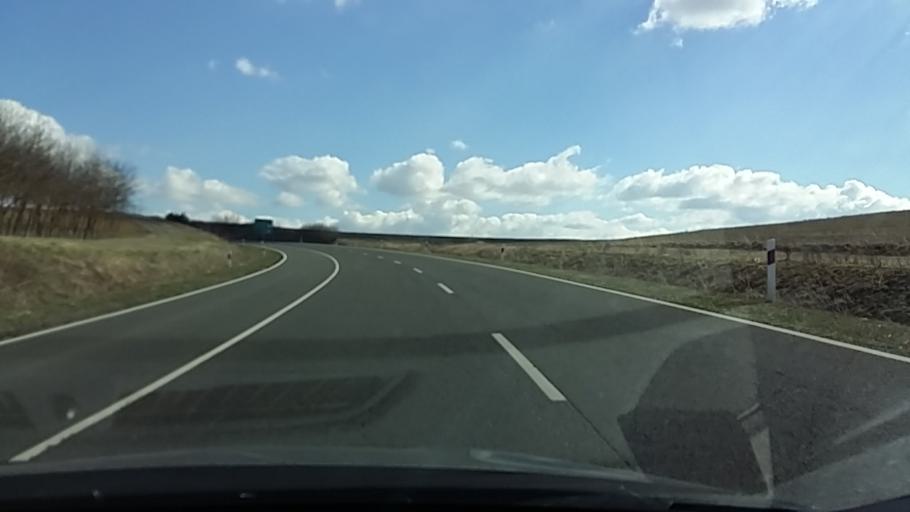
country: HU
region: Baranya
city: Kozarmisleny
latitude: 46.0236
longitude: 18.2813
